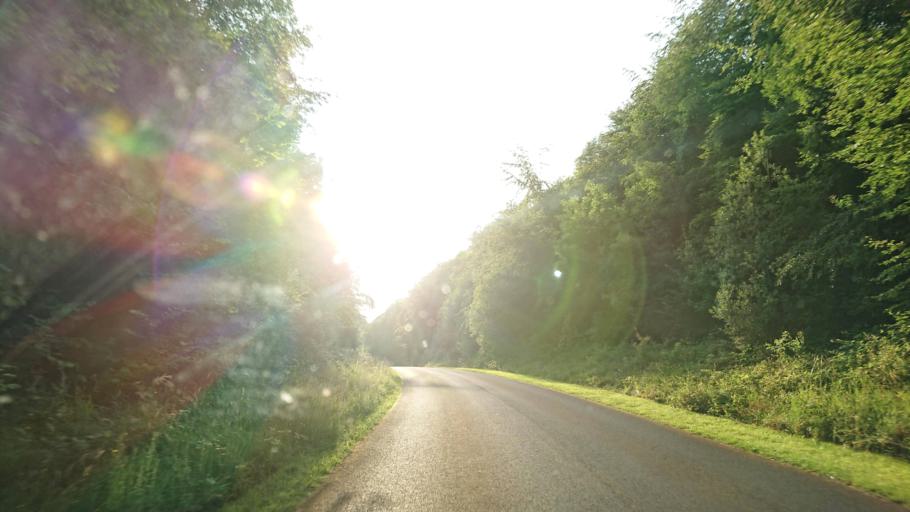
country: IE
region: Connaught
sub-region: Roscommon
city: Boyle
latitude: 53.9770
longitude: -8.2429
